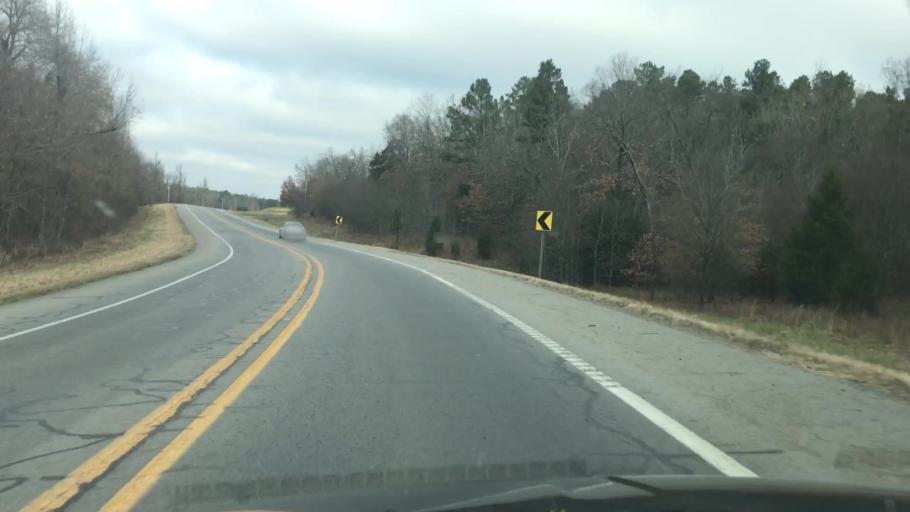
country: US
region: Arkansas
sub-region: Scott County
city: Waldron
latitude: 34.8239
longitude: -94.0364
